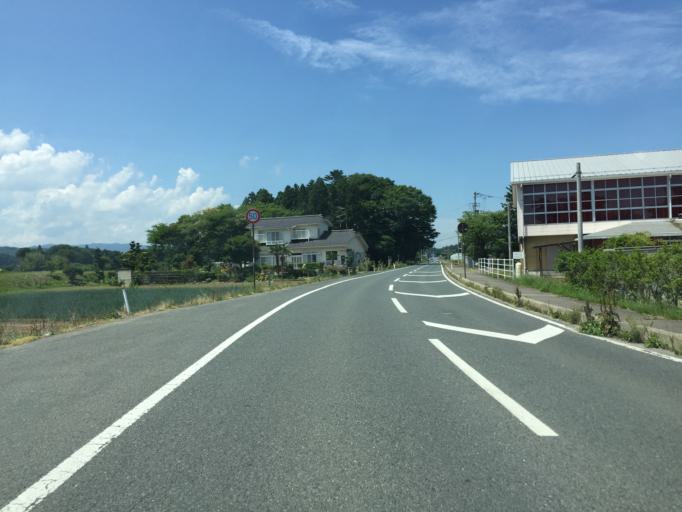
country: JP
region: Miyagi
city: Marumori
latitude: 37.7254
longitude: 140.9303
